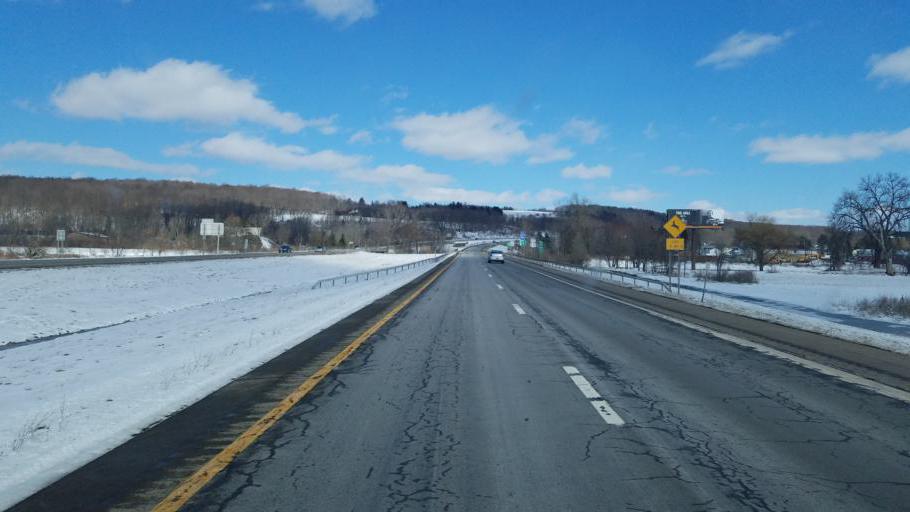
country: US
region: New York
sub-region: Chautauqua County
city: Falconer
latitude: 42.1329
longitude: -79.1850
